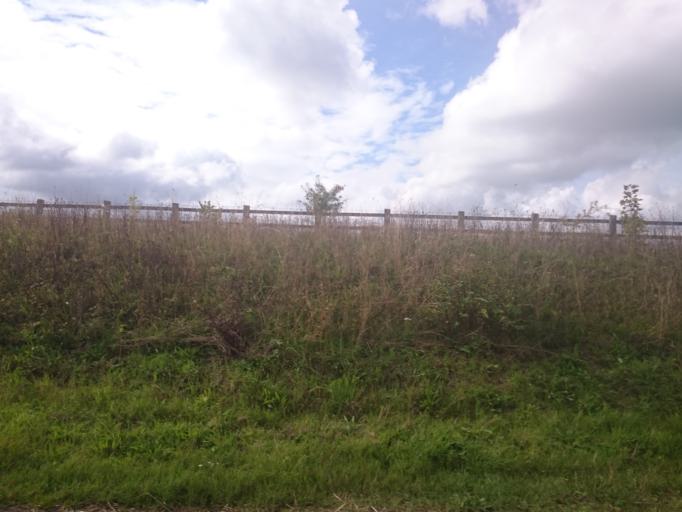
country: GB
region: England
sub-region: Gloucestershire
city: Coates
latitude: 51.7787
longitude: -2.0336
